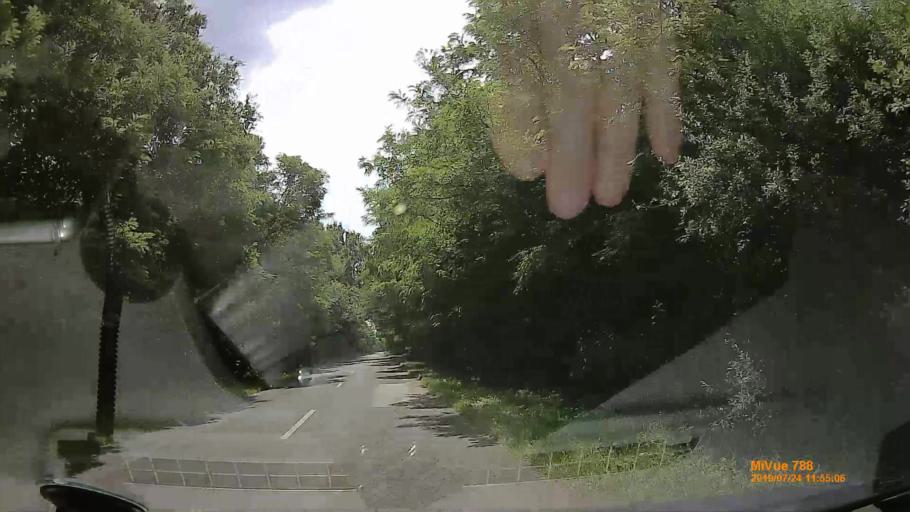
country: HU
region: Szabolcs-Szatmar-Bereg
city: Vasarosnameny
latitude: 48.2126
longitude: 22.4128
